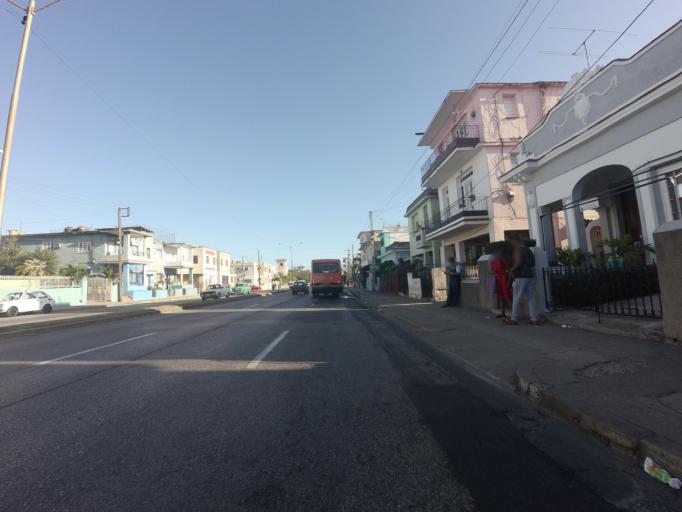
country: CU
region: La Habana
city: Cerro
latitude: 23.1100
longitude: -82.4242
